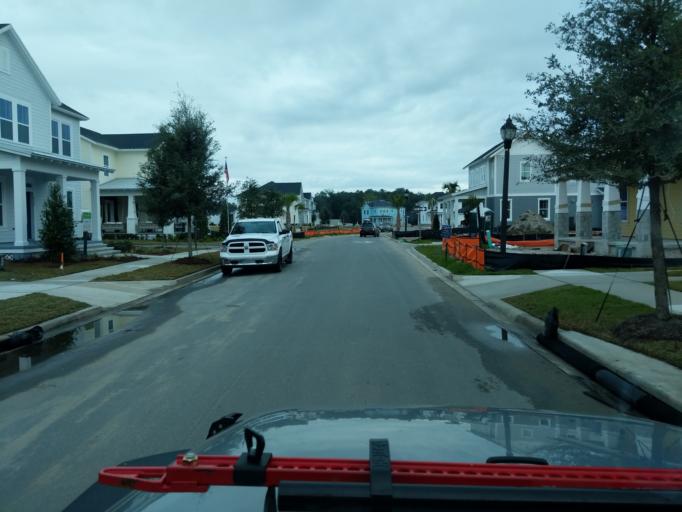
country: US
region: Florida
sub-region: Orange County
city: Oakland
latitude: 28.5559
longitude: -81.6158
